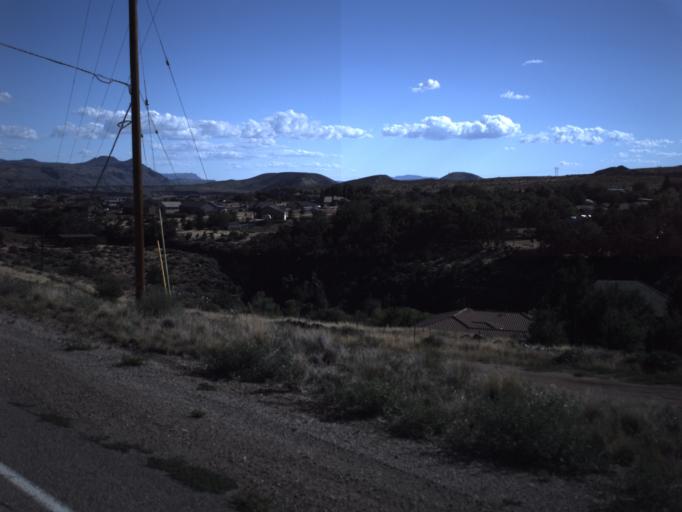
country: US
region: Utah
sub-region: Washington County
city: Toquerville
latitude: 37.2448
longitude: -113.2835
